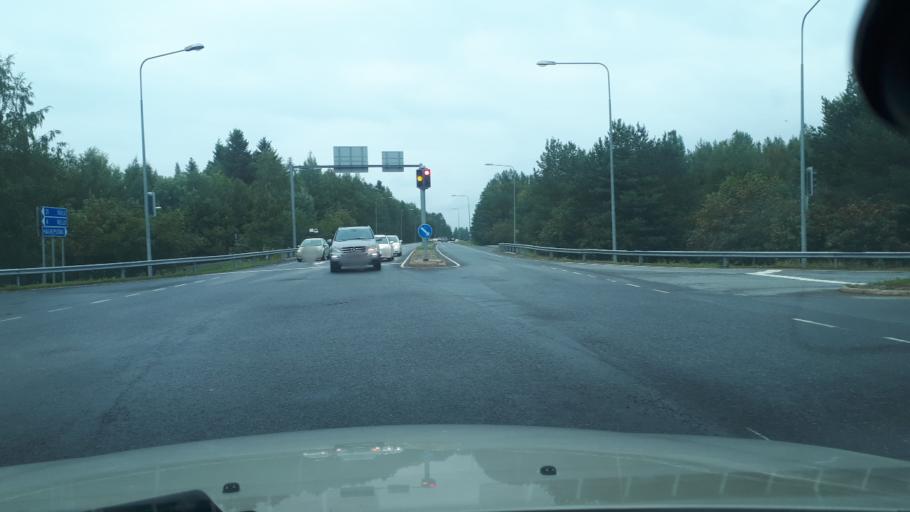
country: FI
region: Northern Ostrobothnia
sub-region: Oulu
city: Haukipudas
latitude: 65.1664
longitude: 25.3474
